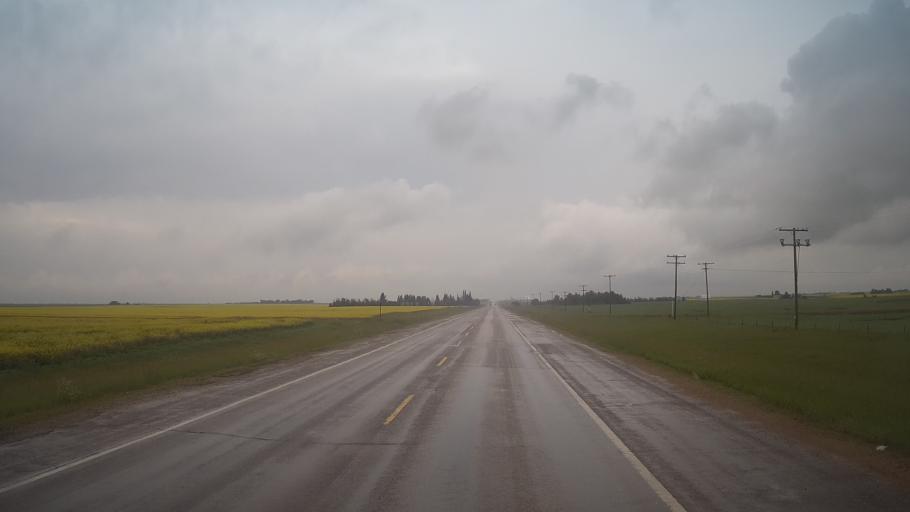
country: CA
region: Saskatchewan
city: Unity
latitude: 52.4349
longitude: -109.0235
